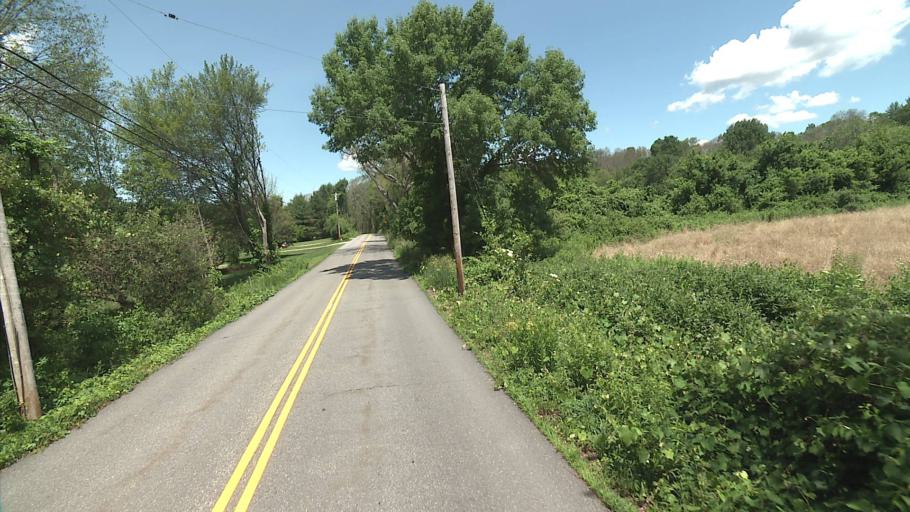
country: US
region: Connecticut
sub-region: New London County
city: Jewett City
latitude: 41.6051
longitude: -71.9109
